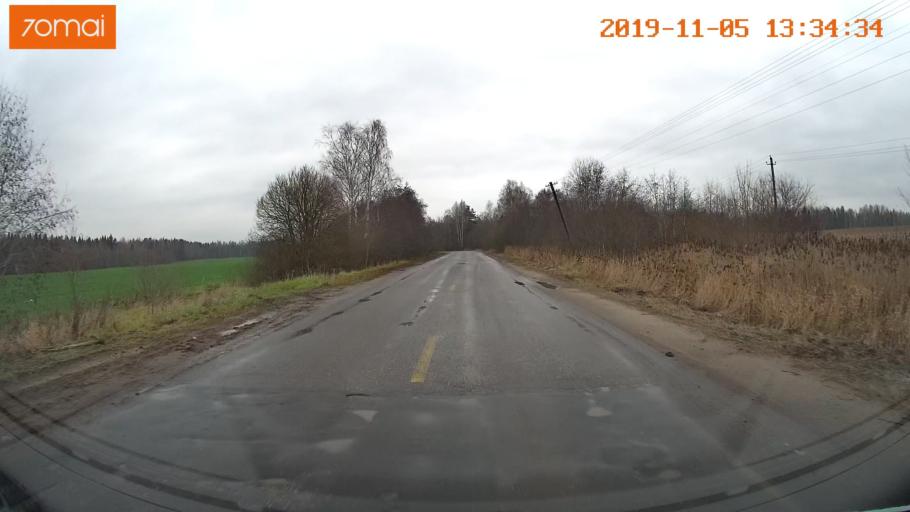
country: RU
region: Ivanovo
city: Shuya
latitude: 56.9017
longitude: 41.3899
